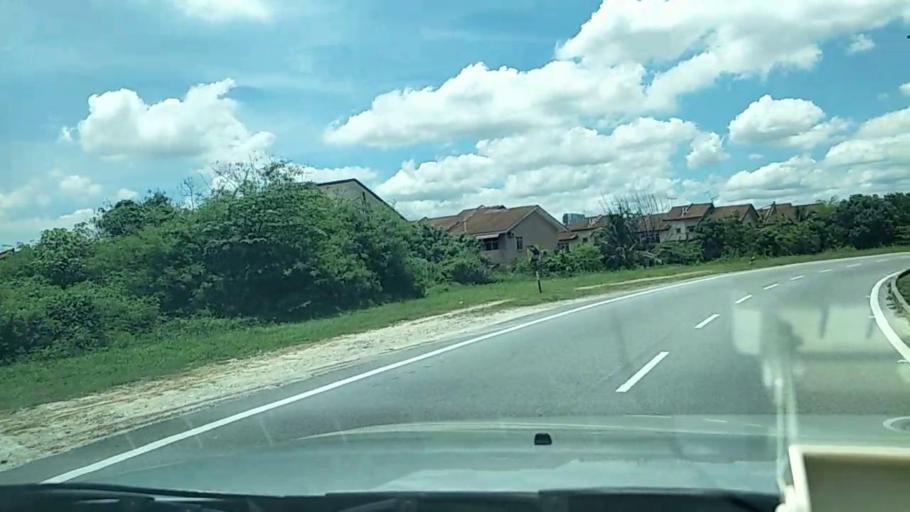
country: MY
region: Selangor
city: Subang Jaya
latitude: 2.9747
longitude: 101.6117
